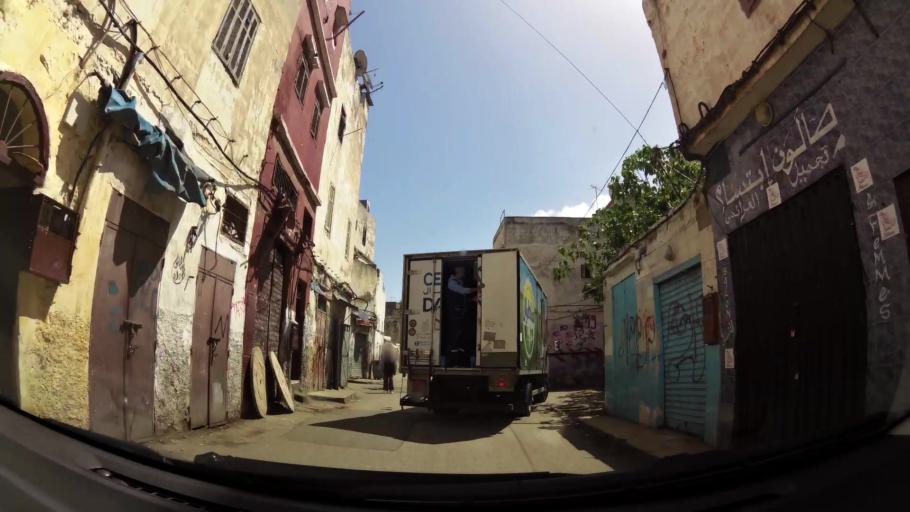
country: MA
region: Grand Casablanca
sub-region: Casablanca
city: Casablanca
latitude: 33.5999
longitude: -7.6266
